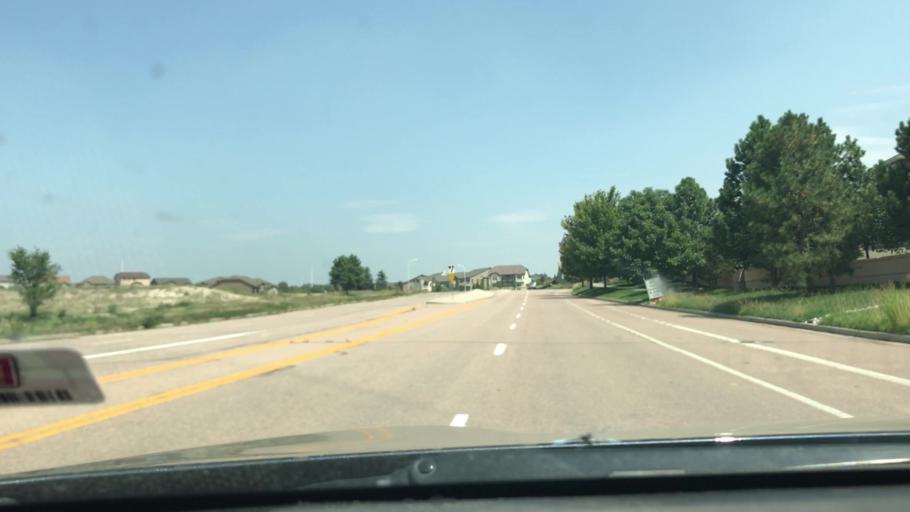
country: US
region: Colorado
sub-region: El Paso County
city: Black Forest
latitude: 38.9821
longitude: -104.7740
